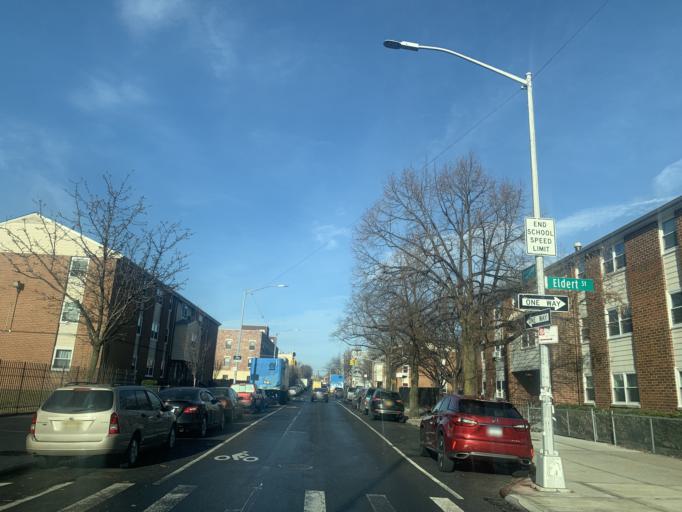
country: US
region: New York
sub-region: Kings County
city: East New York
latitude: 40.6881
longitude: -73.9115
